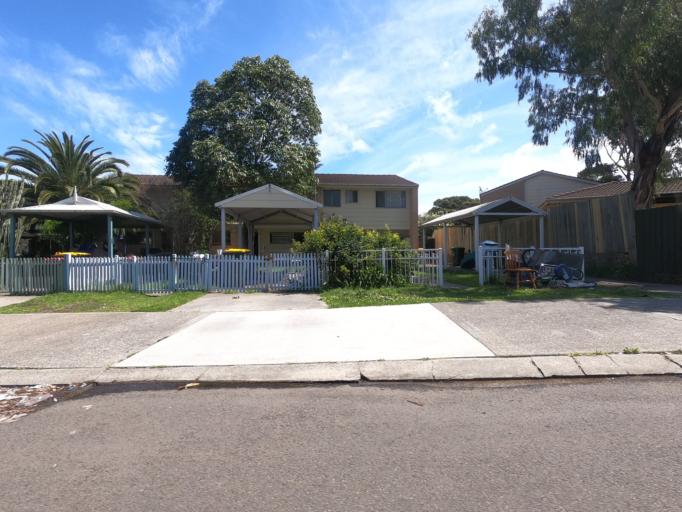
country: AU
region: New South Wales
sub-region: Wollongong
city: Lake Heights
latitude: -34.4901
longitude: 150.8762
